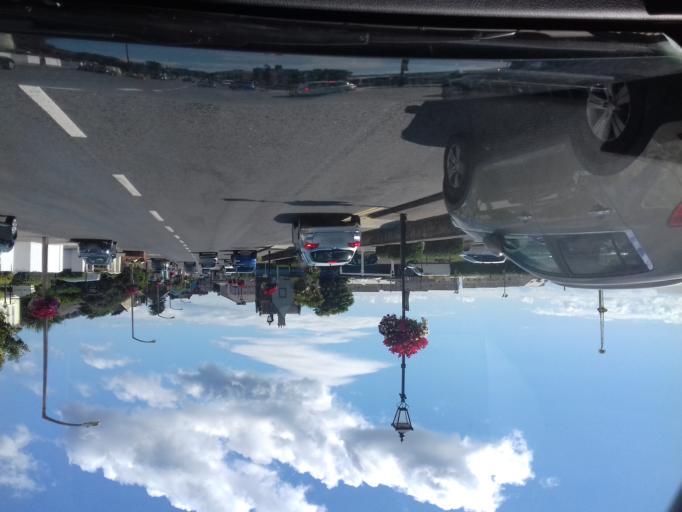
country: IE
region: Munster
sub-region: Waterford
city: Tra Mhor
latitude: 52.1631
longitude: -7.1478
